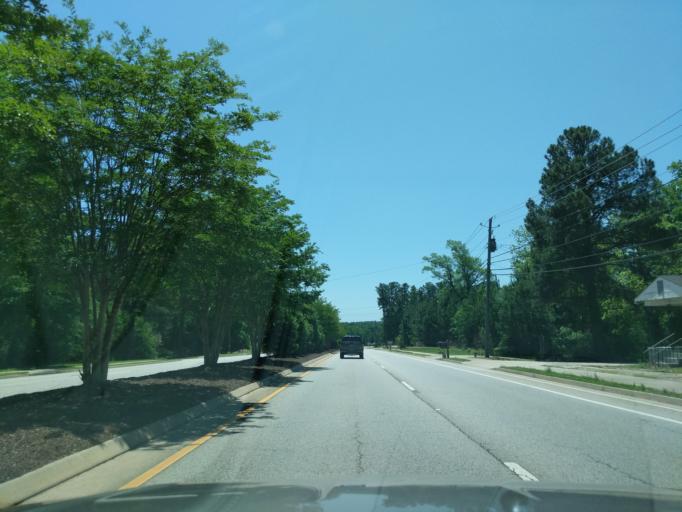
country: US
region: Georgia
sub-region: Columbia County
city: Martinez
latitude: 33.5482
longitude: -82.0887
